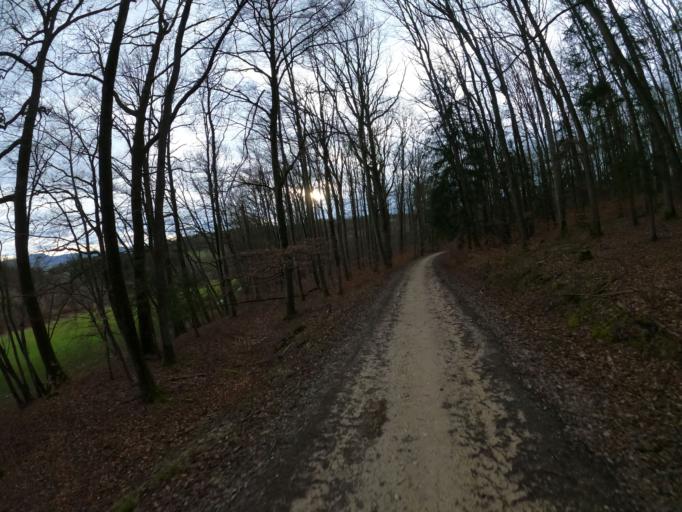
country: DE
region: Baden-Wuerttemberg
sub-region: Regierungsbezirk Stuttgart
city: Eislingen
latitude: 48.7201
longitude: 9.7169
